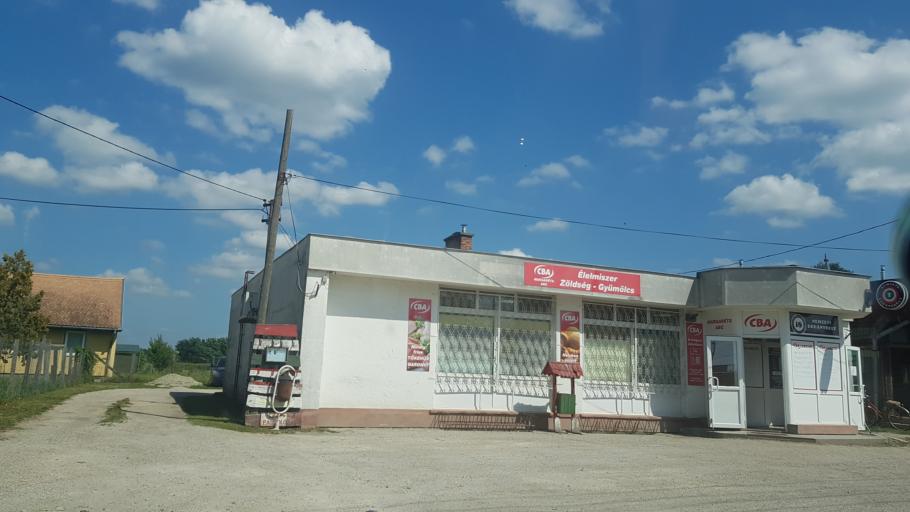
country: HU
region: Somogy
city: Marcali
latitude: 46.4960
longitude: 17.4229
